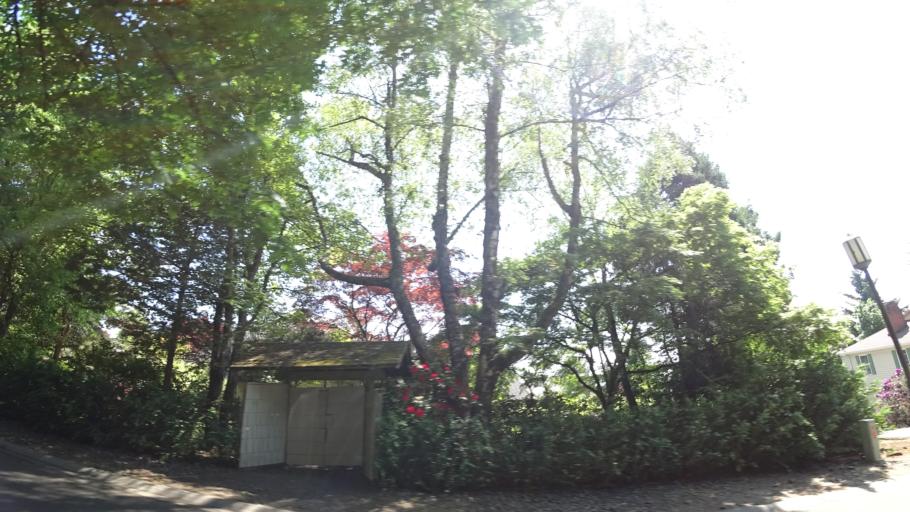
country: US
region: Oregon
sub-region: Clackamas County
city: Lake Oswego
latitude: 45.4309
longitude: -122.7140
